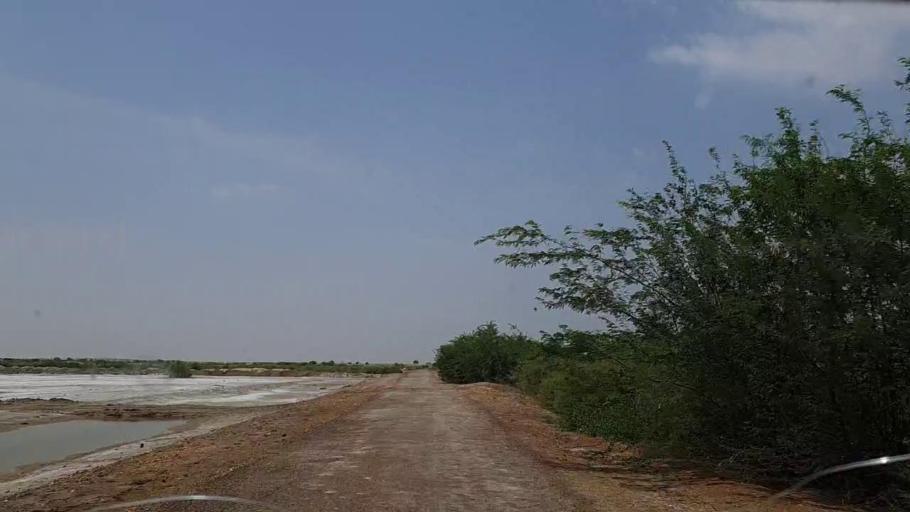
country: PK
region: Sindh
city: Phulji
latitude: 26.8696
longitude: 67.6528
